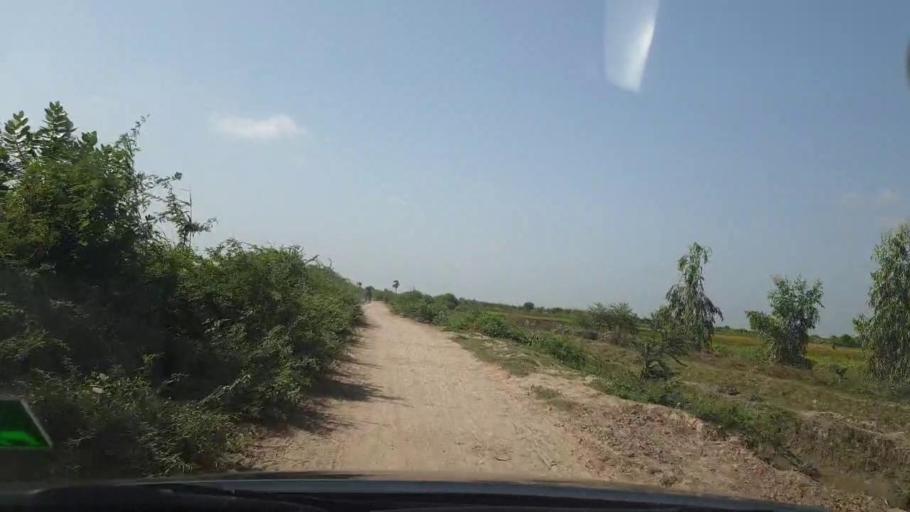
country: PK
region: Sindh
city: Tando Bago
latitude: 24.7662
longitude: 68.9438
